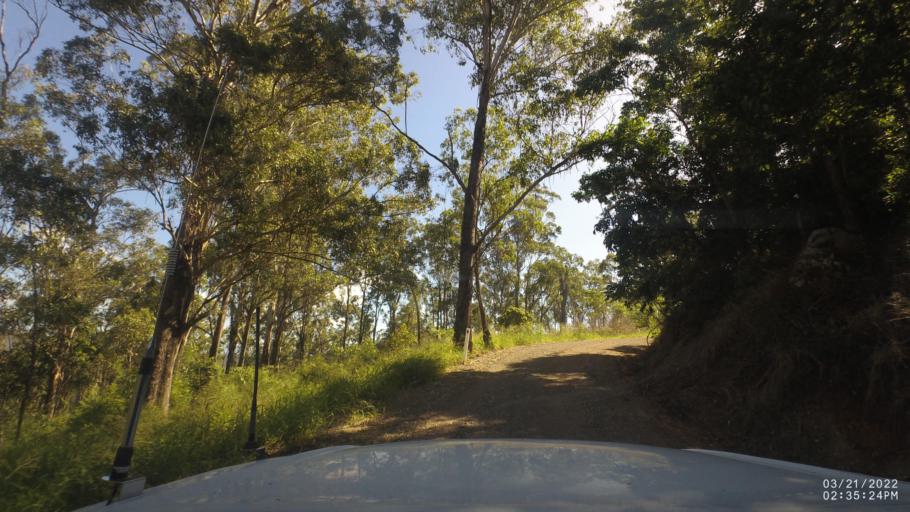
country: AU
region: Queensland
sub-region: Ipswich
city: Deebing Heights
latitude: -27.8291
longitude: 152.8195
